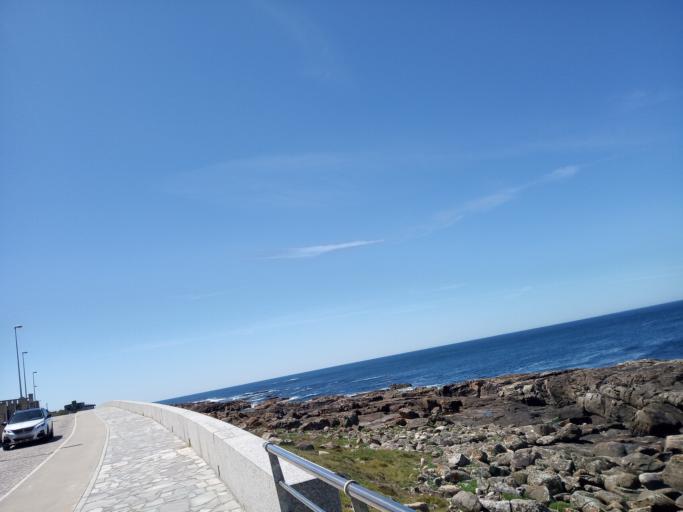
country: ES
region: Galicia
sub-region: Provincia de Pontevedra
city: A Guarda
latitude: 41.8916
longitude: -8.8801
